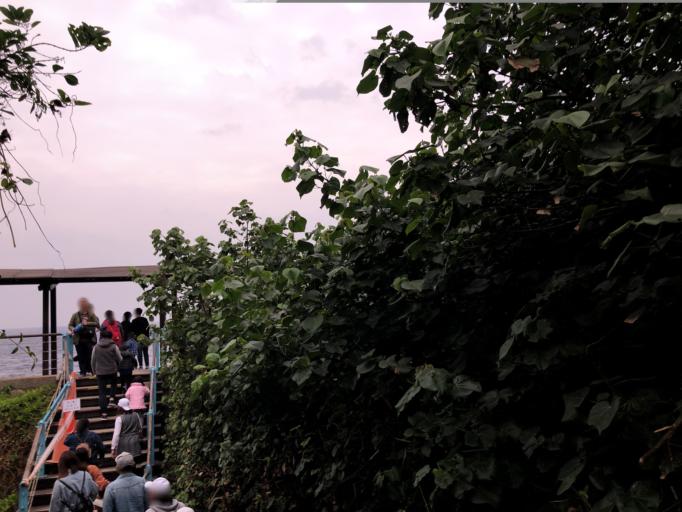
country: TW
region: Kaohsiung
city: Kaohsiung
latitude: 22.3297
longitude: 120.3546
